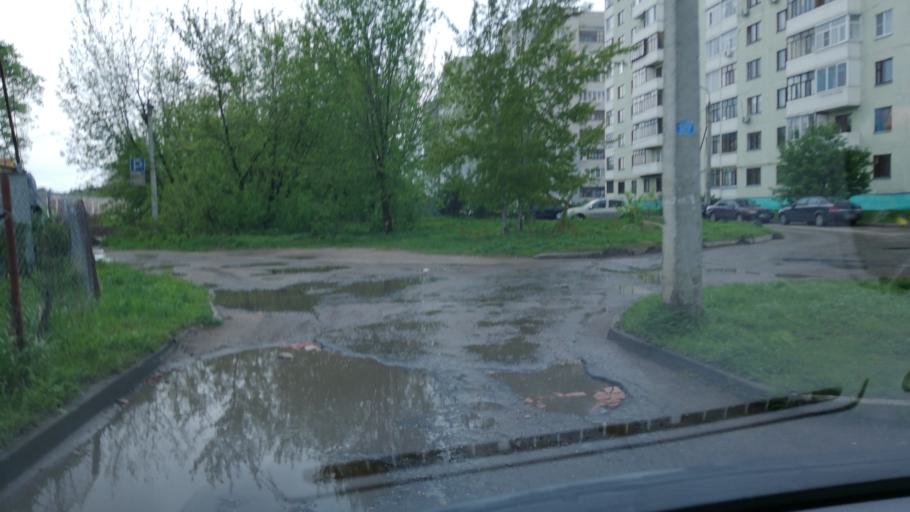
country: RU
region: Jaroslavl
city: Yaroslavl
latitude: 57.6571
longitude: 39.9242
